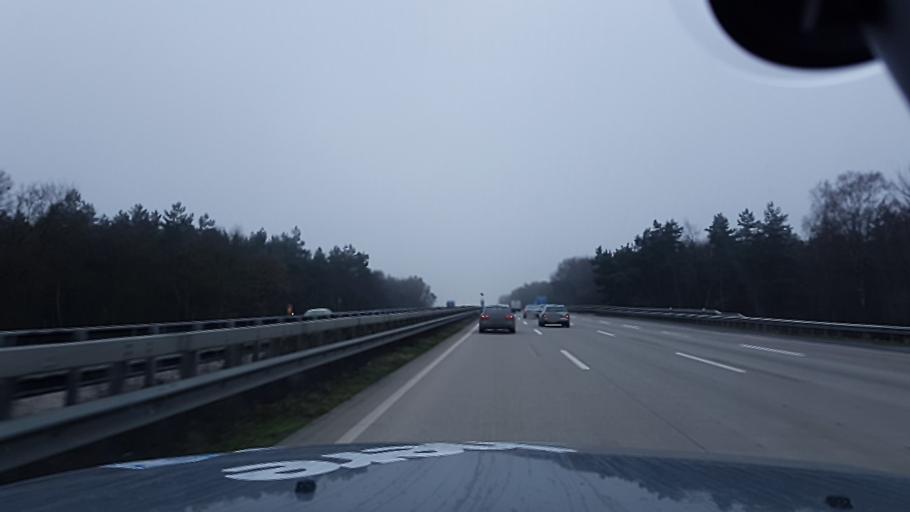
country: DE
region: Lower Saxony
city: Buehren
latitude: 52.8571
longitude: 8.2308
